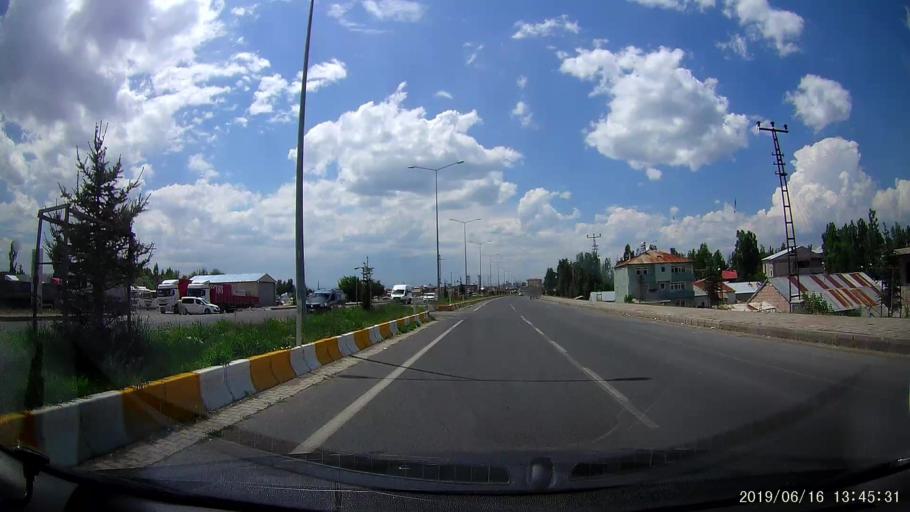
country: TR
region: Agri
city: Agri
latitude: 39.7090
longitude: 43.0449
